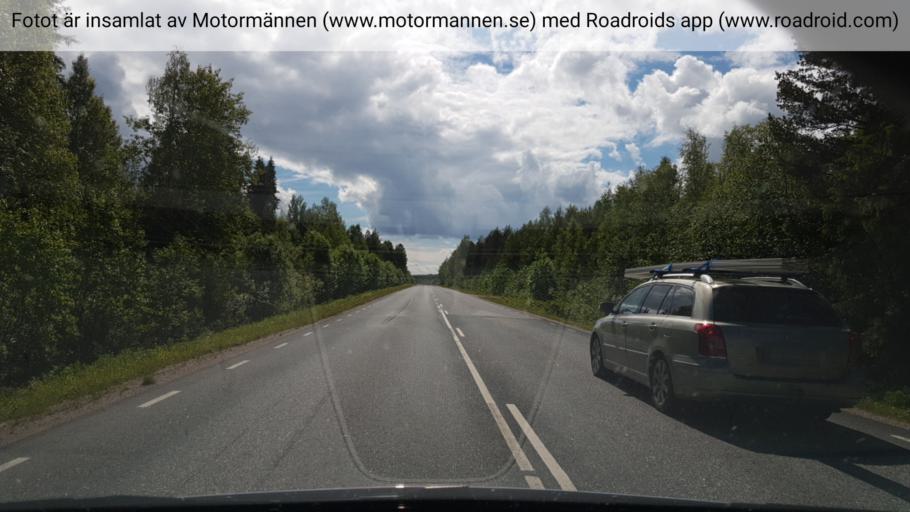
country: FI
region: Lapland
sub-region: Torniolaakso
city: Ylitornio
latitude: 66.3124
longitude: 23.6208
